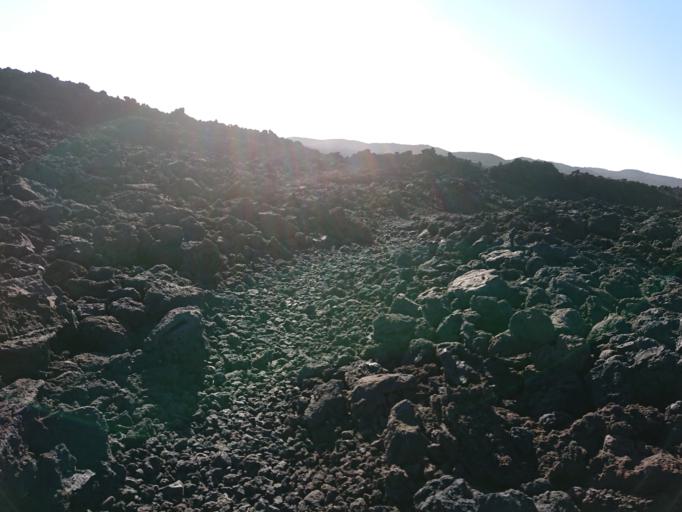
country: ES
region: Canary Islands
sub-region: Provincia de Las Palmas
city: Tinajo
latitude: 29.0809
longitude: -13.7297
